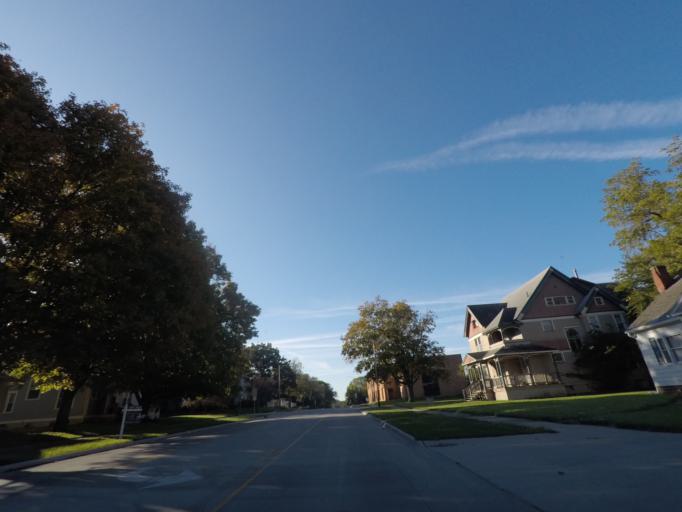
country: US
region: Iowa
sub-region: Story County
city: Nevada
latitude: 42.0181
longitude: -93.4523
